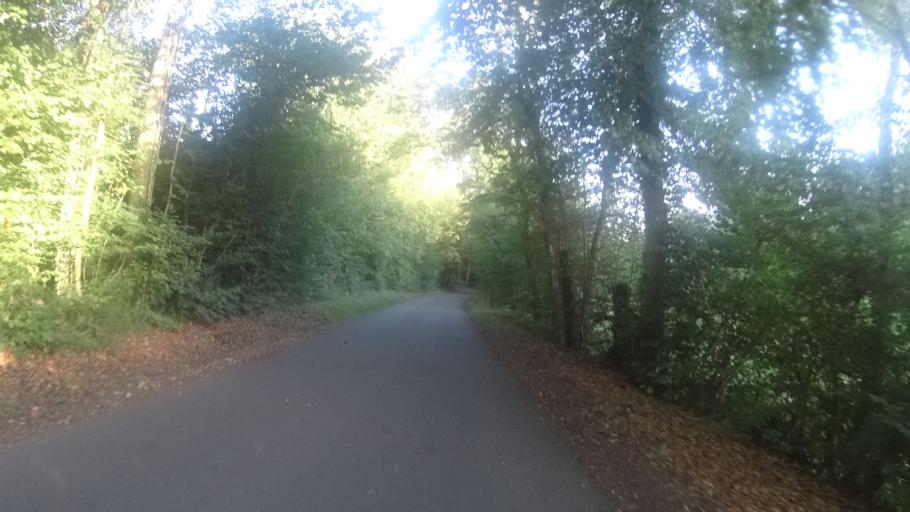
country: FR
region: Picardie
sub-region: Departement de l'Oise
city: Ver-sur-Launette
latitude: 49.1754
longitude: 2.6773
